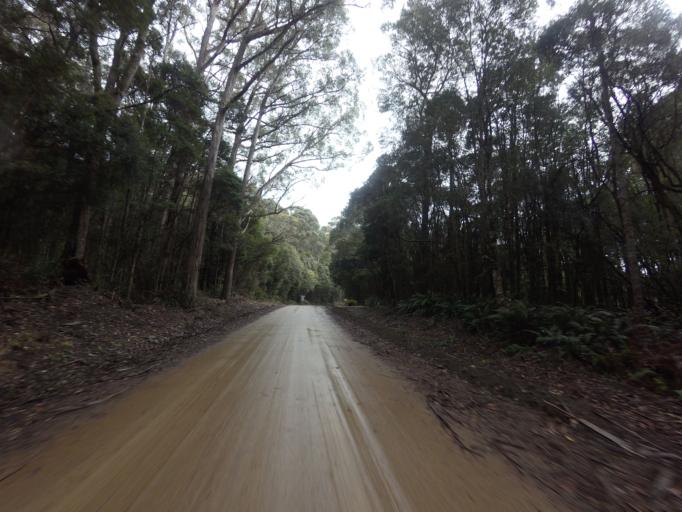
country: AU
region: Tasmania
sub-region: Huon Valley
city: Geeveston
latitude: -43.5586
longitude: 146.8904
